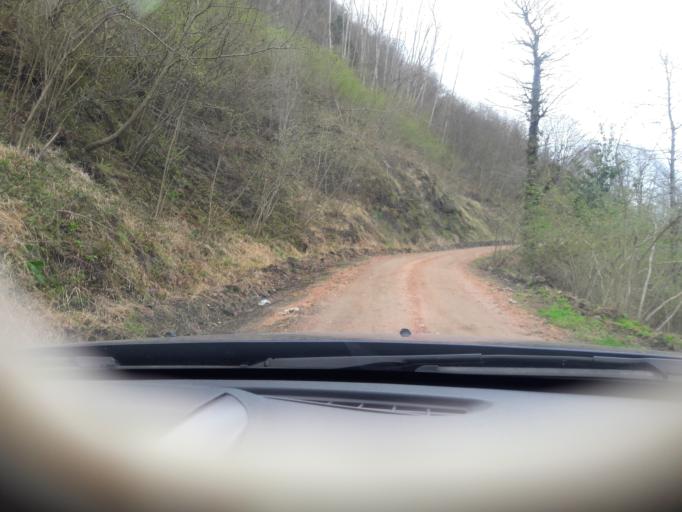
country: TR
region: Trabzon
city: Salpazari
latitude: 40.9716
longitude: 39.1971
